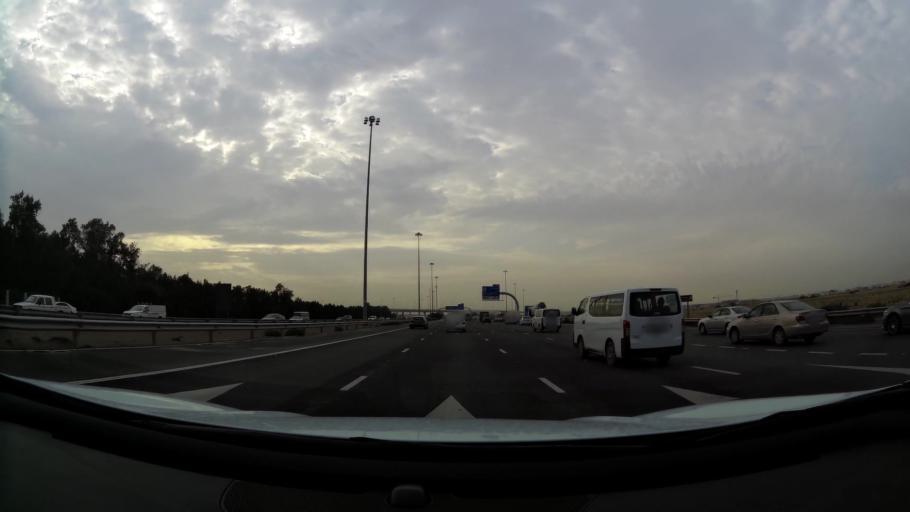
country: AE
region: Abu Dhabi
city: Abu Dhabi
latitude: 24.3172
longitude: 54.5929
